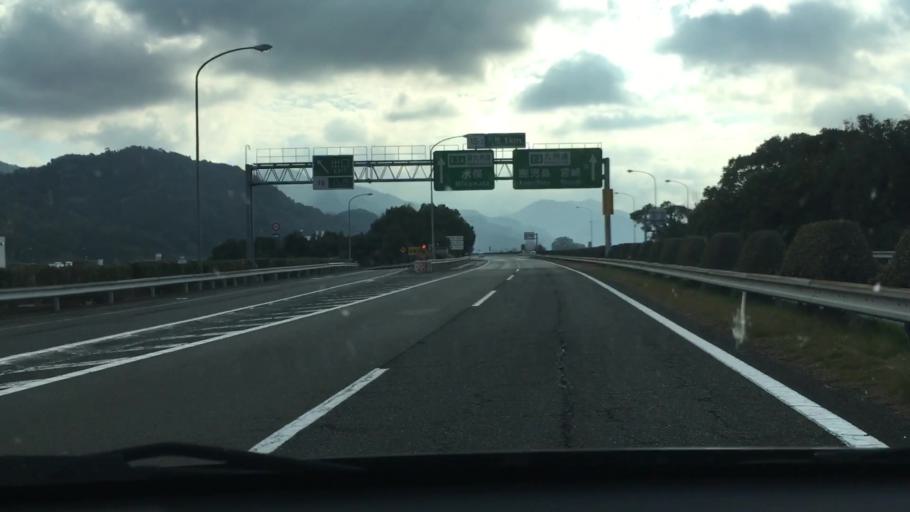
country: JP
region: Kumamoto
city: Yatsushiro
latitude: 32.5143
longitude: 130.6486
